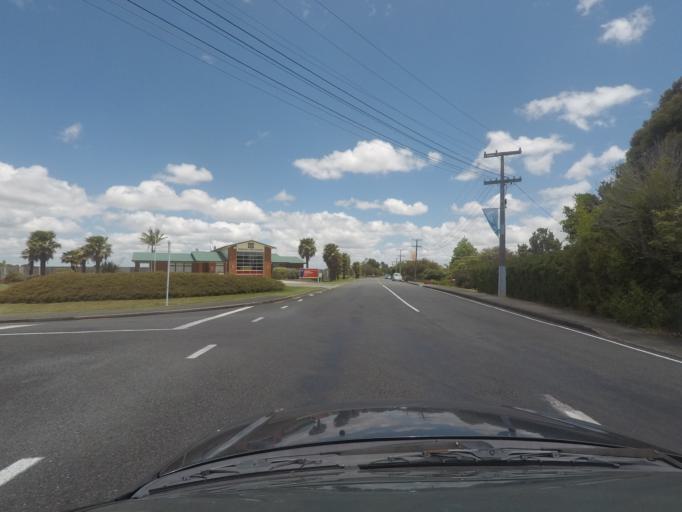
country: NZ
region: Northland
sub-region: Whangarei
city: Whangarei
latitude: -35.7648
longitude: 174.3670
